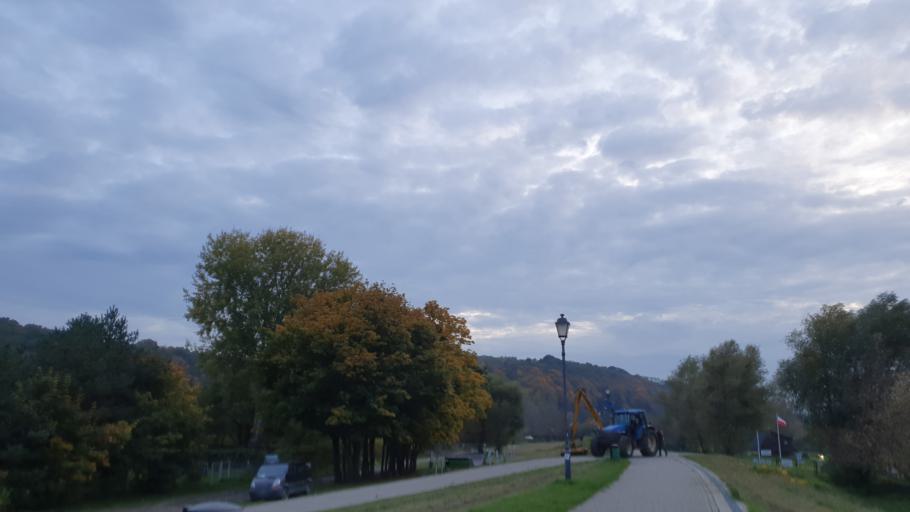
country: PL
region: Lublin Voivodeship
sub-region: Powiat pulawski
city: Kazimierz Dolny
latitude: 51.3239
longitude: 21.9439
